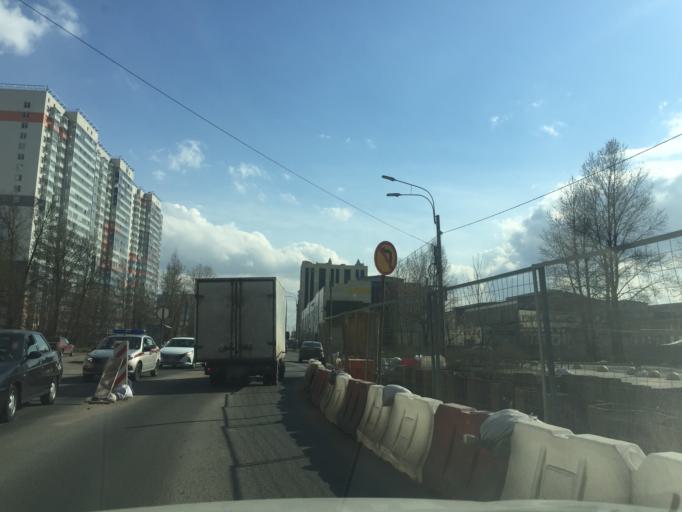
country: RU
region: St.-Petersburg
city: Krasnogvargeisky
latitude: 59.9399
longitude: 30.4351
